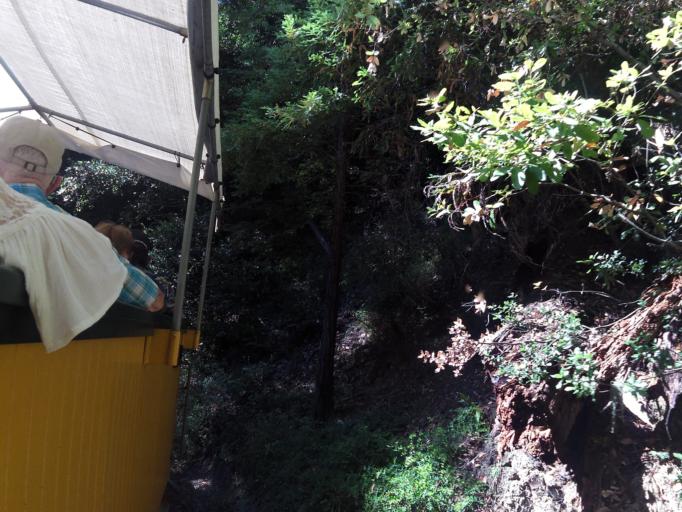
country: US
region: California
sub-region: Santa Cruz County
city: Mount Hermon
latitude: 37.0430
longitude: -122.0586
